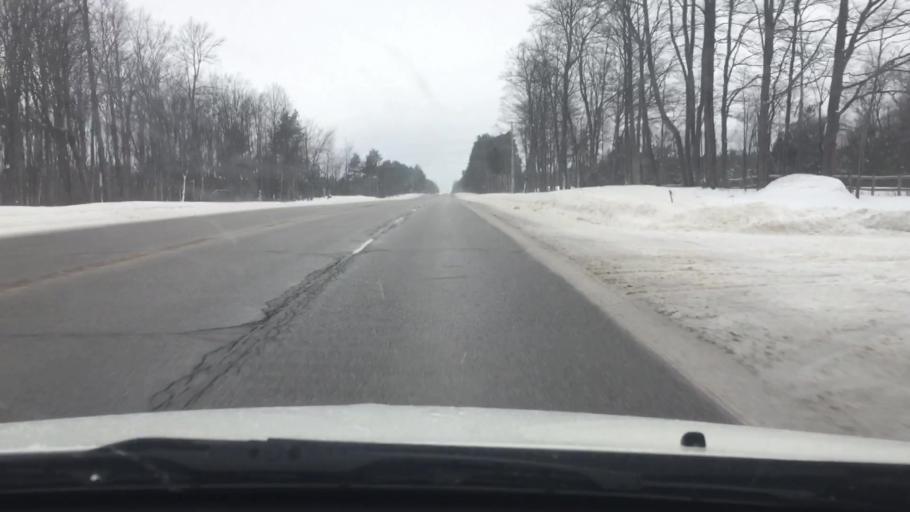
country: US
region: Michigan
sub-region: Otsego County
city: Gaylord
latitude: 45.0621
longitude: -84.8266
